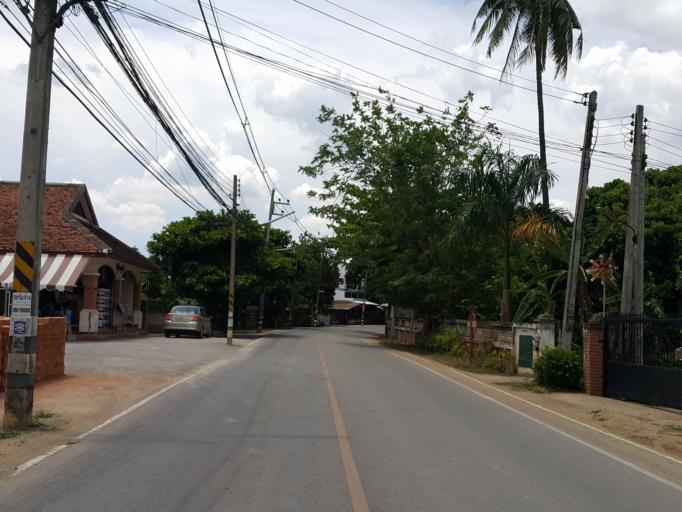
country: TH
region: Chiang Mai
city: Chiang Mai
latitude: 18.7498
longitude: 98.9921
